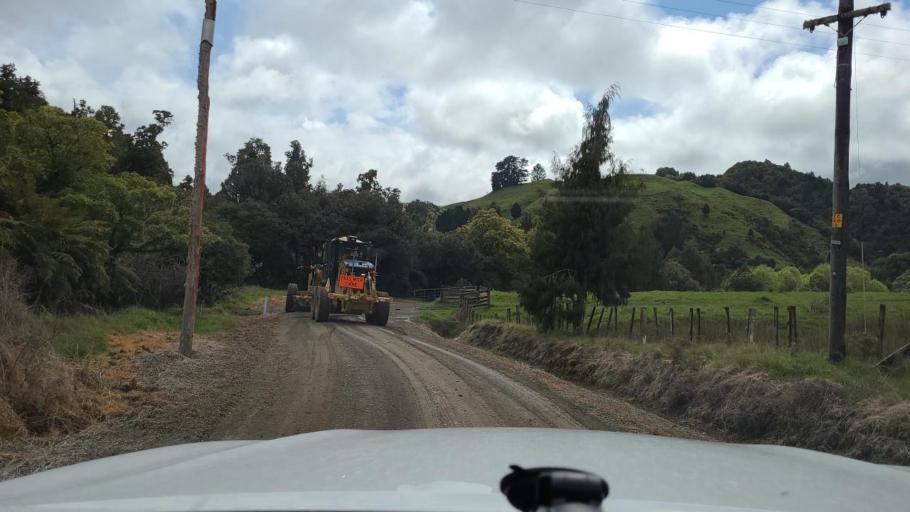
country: NZ
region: Bay of Plenty
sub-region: Opotiki District
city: Opotiki
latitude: -38.2521
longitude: 177.6033
